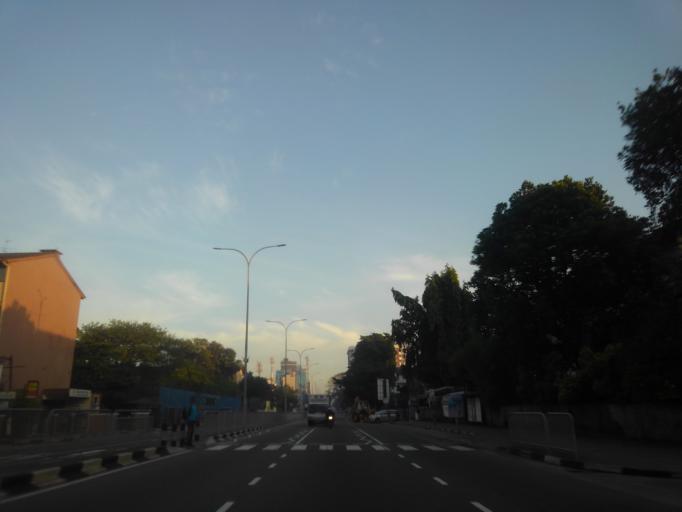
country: LK
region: Western
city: Pita Kotte
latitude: 6.9006
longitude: 79.8773
